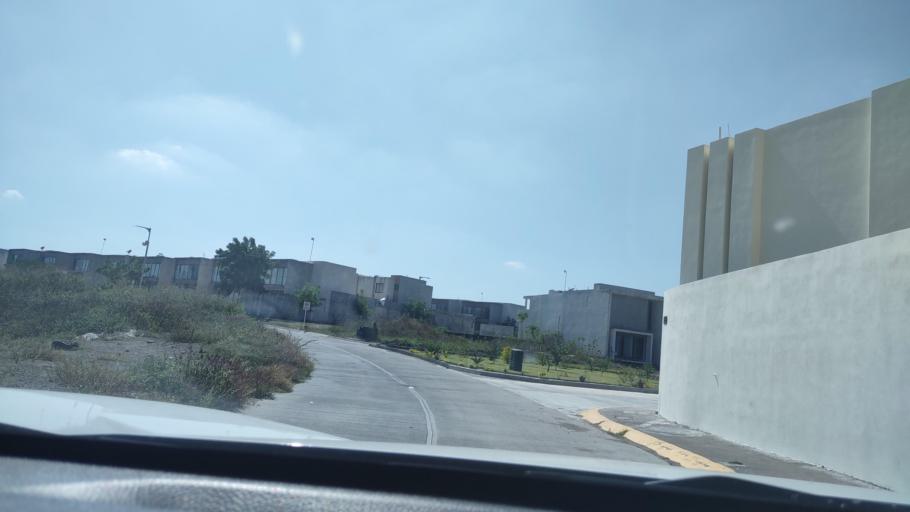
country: MX
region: Veracruz
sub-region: Veracruz
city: Fraccionamiento Geovillas los Pinos
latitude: 19.2195
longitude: -96.2337
